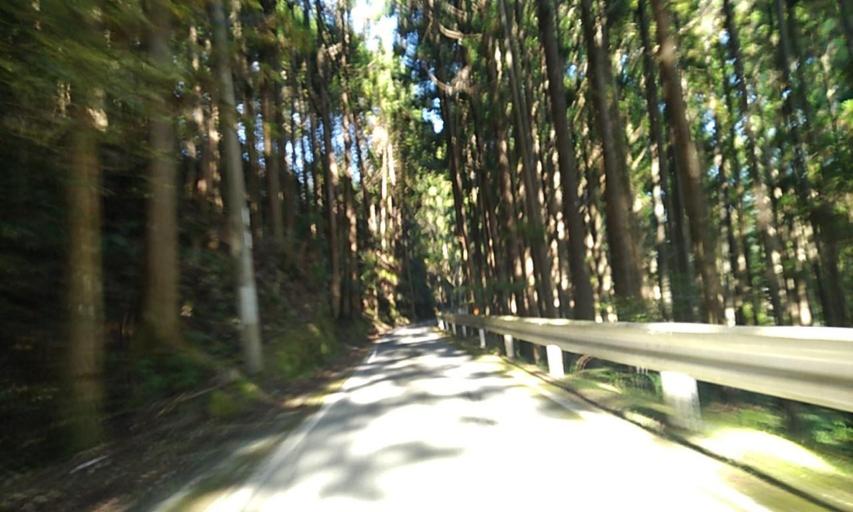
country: JP
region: Wakayama
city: Shingu
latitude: 33.9159
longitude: 135.9890
